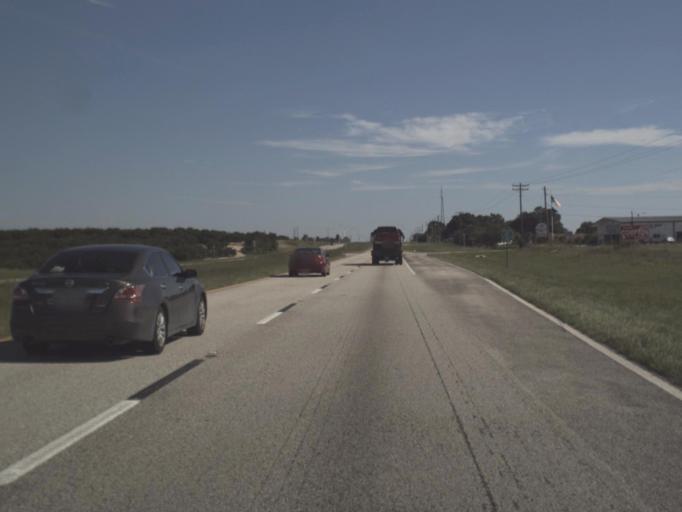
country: US
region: Florida
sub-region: Highlands County
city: Lake Placid
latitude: 27.3283
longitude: -81.3787
